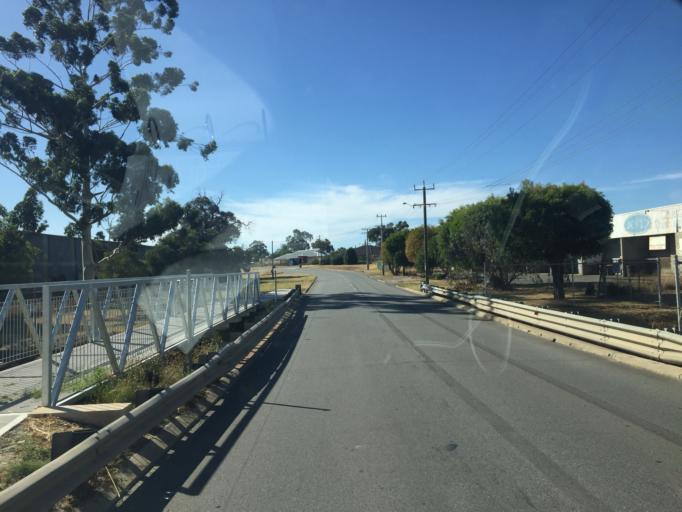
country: AU
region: Western Australia
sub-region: Gosnells
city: Maddington
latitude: -32.0411
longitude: 115.9844
